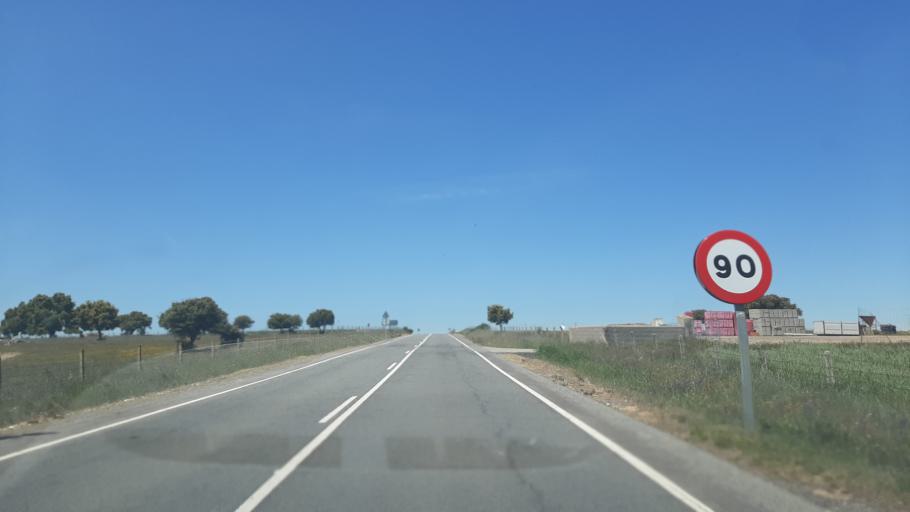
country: ES
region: Castille and Leon
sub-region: Provincia de Salamanca
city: Aldeavieja de Tormes
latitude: 40.5478
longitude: -5.5987
